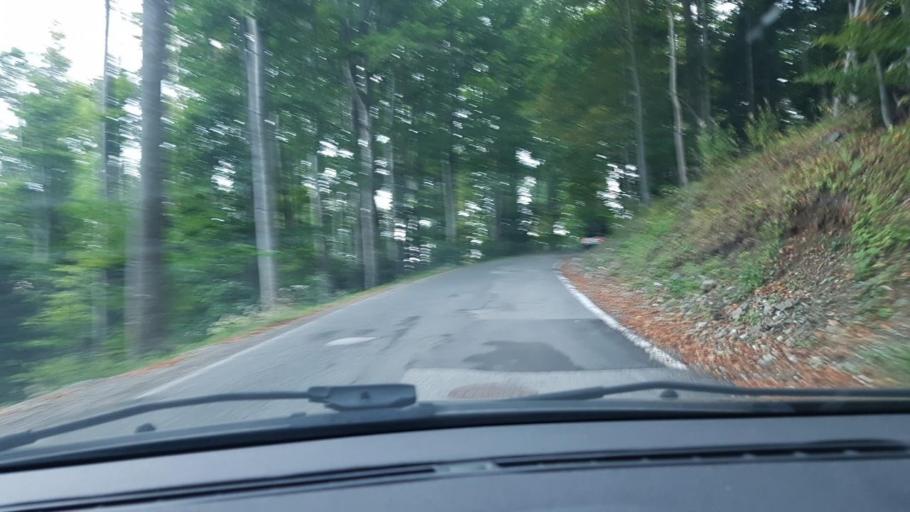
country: HR
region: Grad Zagreb
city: Kasina
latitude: 45.8955
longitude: 15.9527
